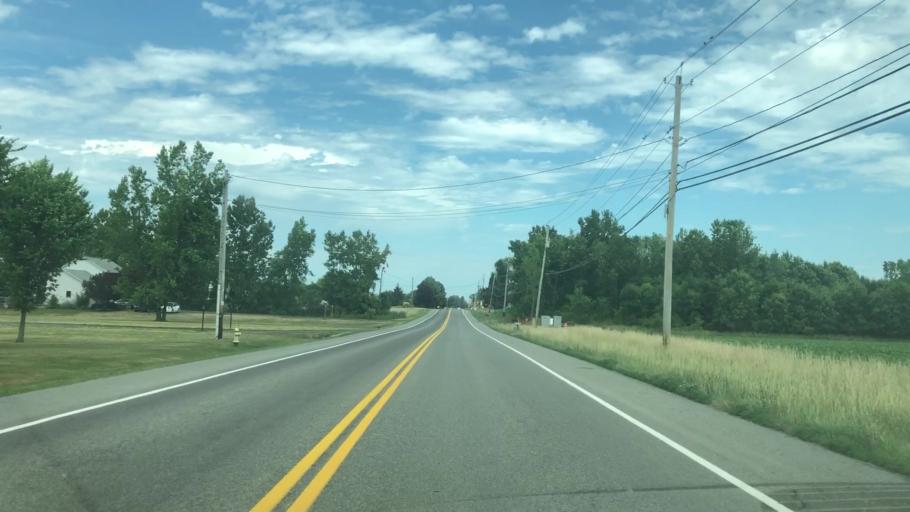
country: US
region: New York
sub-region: Monroe County
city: Webster
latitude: 43.2008
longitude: -77.4005
